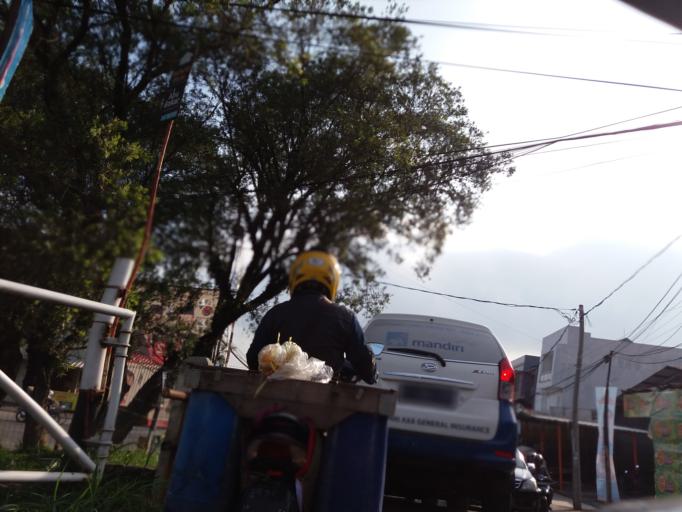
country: ID
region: West Java
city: Bandung
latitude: -6.9516
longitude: 107.6272
